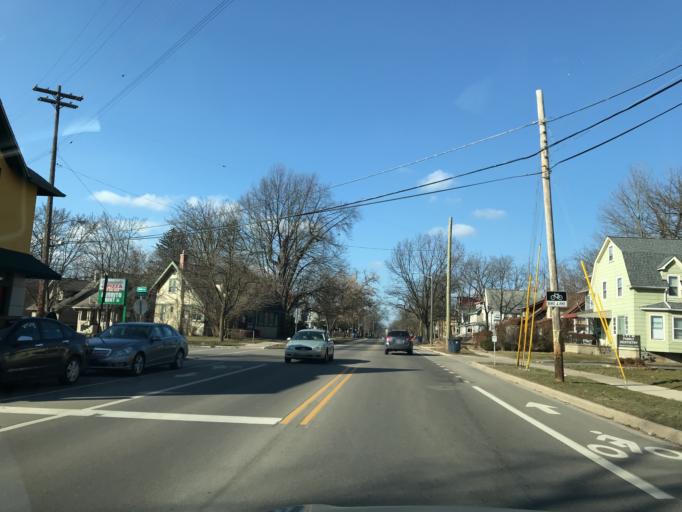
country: US
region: Michigan
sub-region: Washtenaw County
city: Ann Arbor
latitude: 42.2657
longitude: -83.7350
